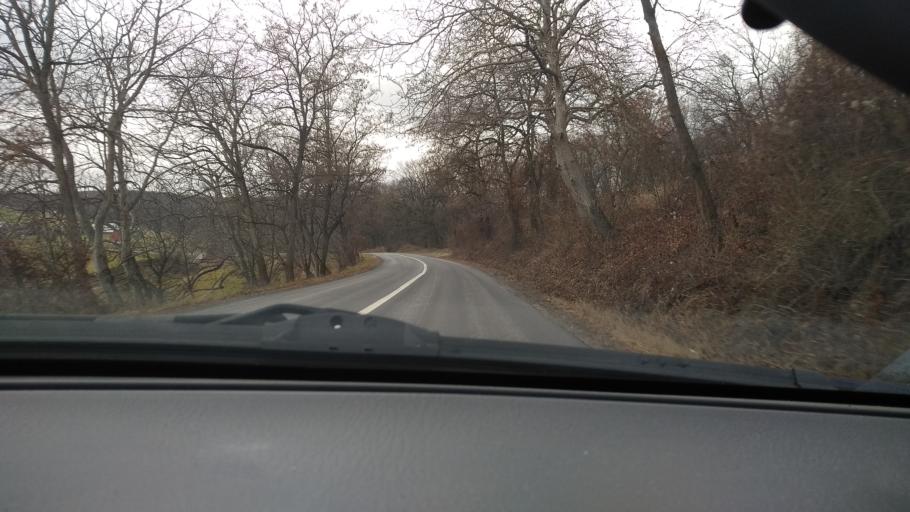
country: RO
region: Mures
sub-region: Comuna Galesti
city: Galesti
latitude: 46.5317
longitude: 24.7092
